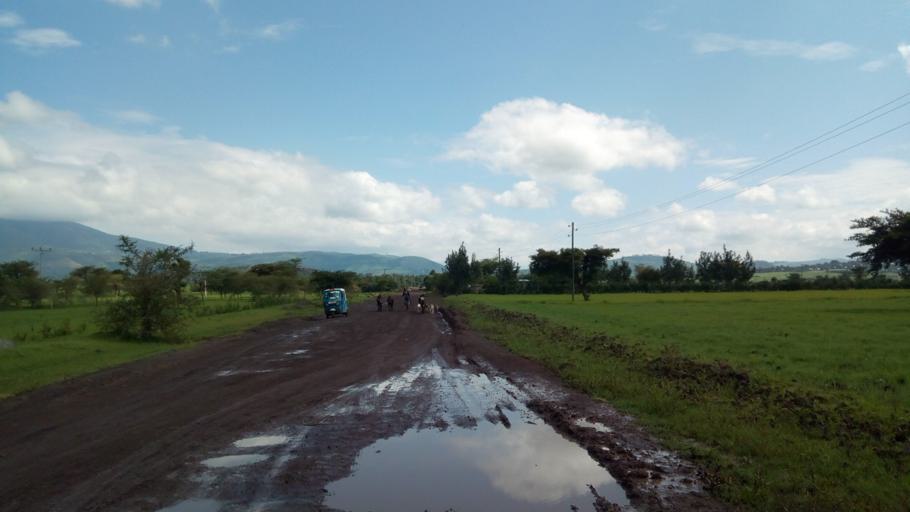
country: ET
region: Oromiya
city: Bishoftu
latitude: 8.8141
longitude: 39.0050
